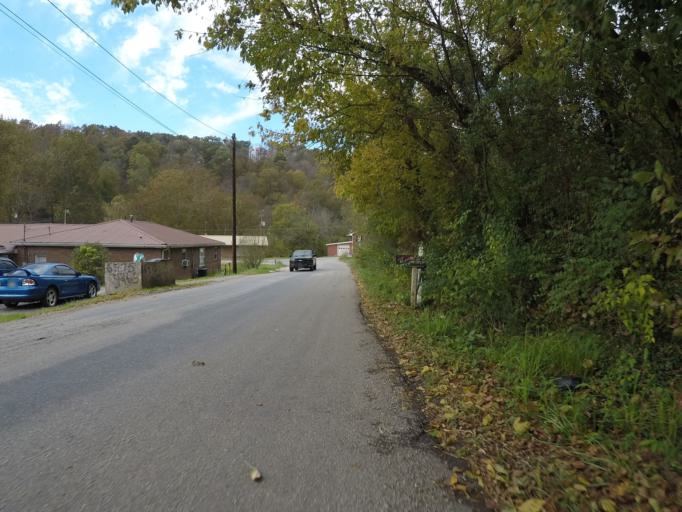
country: US
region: West Virginia
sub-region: Wayne County
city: Lavalette
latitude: 38.3392
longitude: -82.4492
